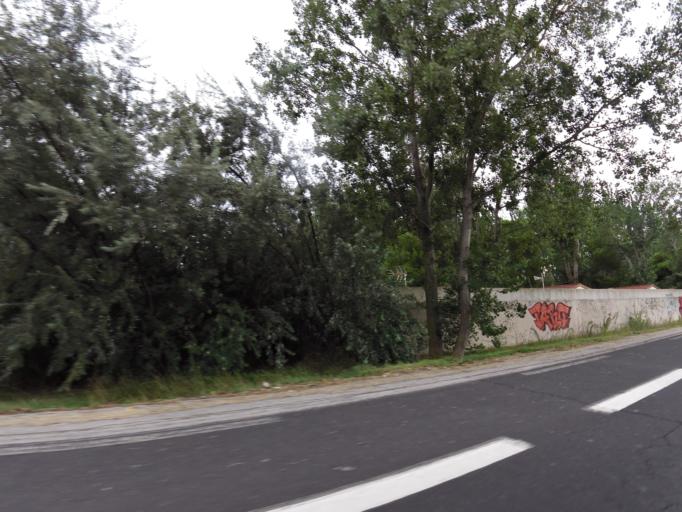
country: FR
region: Languedoc-Roussillon
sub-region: Departement du Gard
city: Le Grau-du-Roi
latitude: 43.5247
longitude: 4.1472
